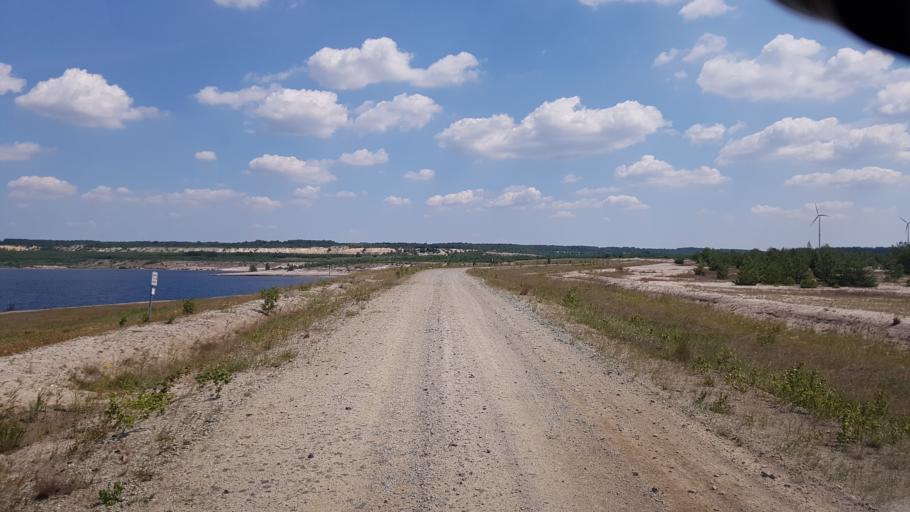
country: DE
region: Brandenburg
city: Sallgast
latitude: 51.5586
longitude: 13.7914
